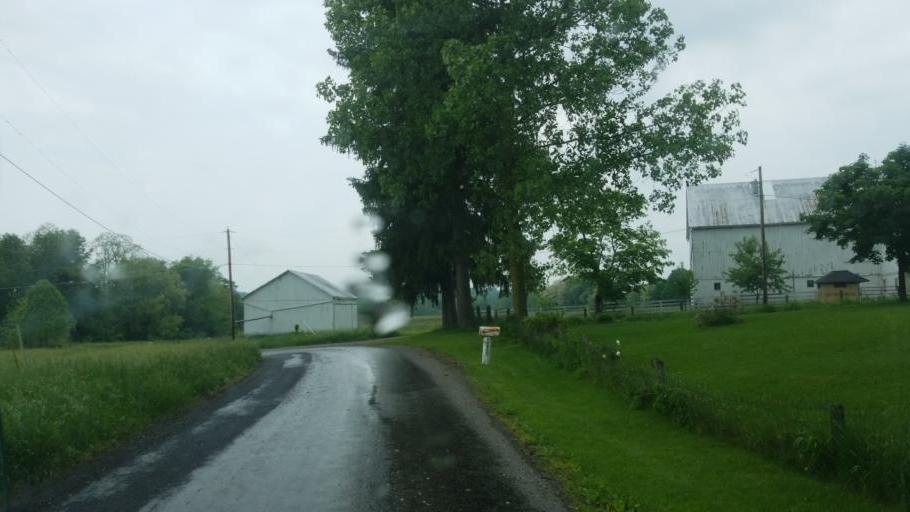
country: US
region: Ohio
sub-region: Wayne County
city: Dalton
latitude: 40.7892
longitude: -81.7206
